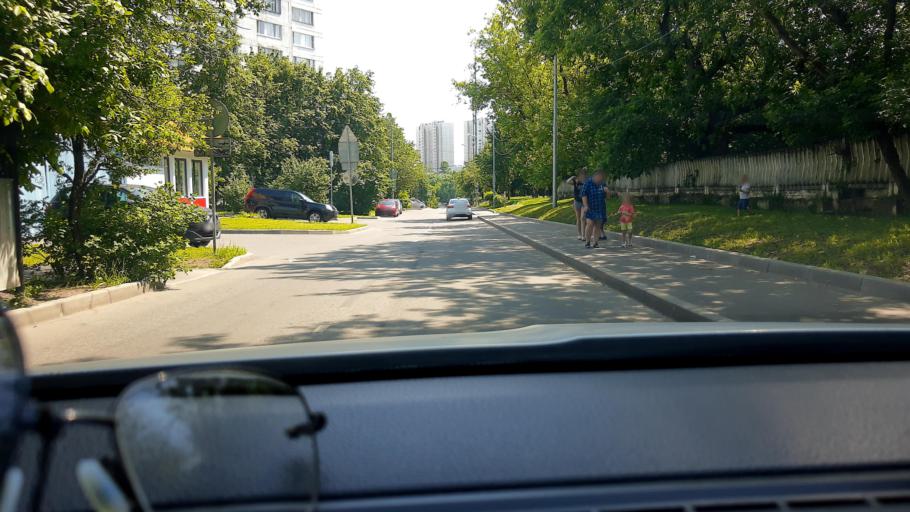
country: RU
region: Moscow
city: Solntsevo
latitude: 55.6573
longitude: 37.3901
